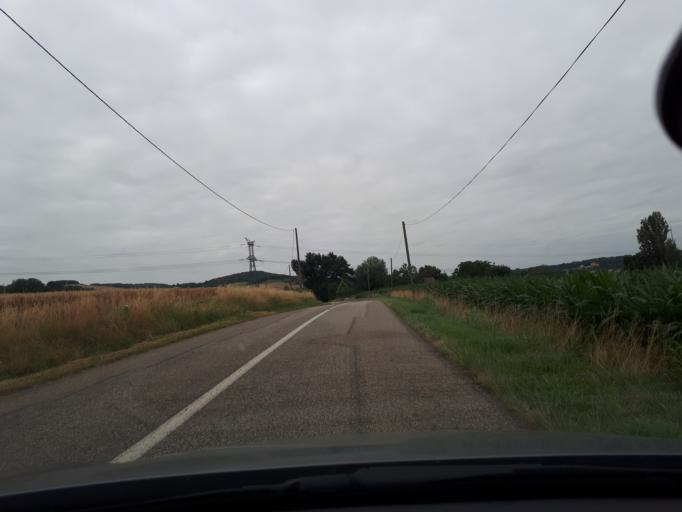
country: FR
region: Midi-Pyrenees
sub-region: Departement du Tarn-et-Garonne
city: Auvillar
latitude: 44.0448
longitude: 0.8572
